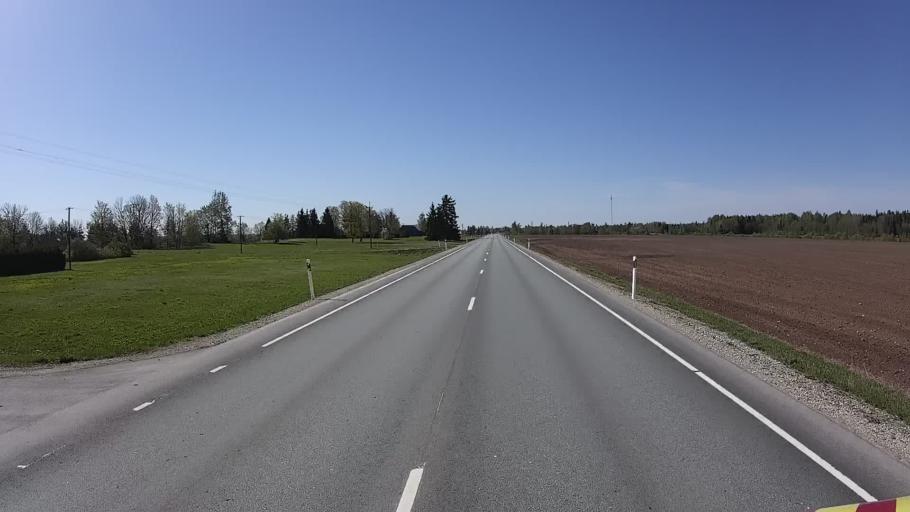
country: EE
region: Paernumaa
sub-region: Tootsi vald
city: Tootsi
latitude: 58.5297
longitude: 24.8296
